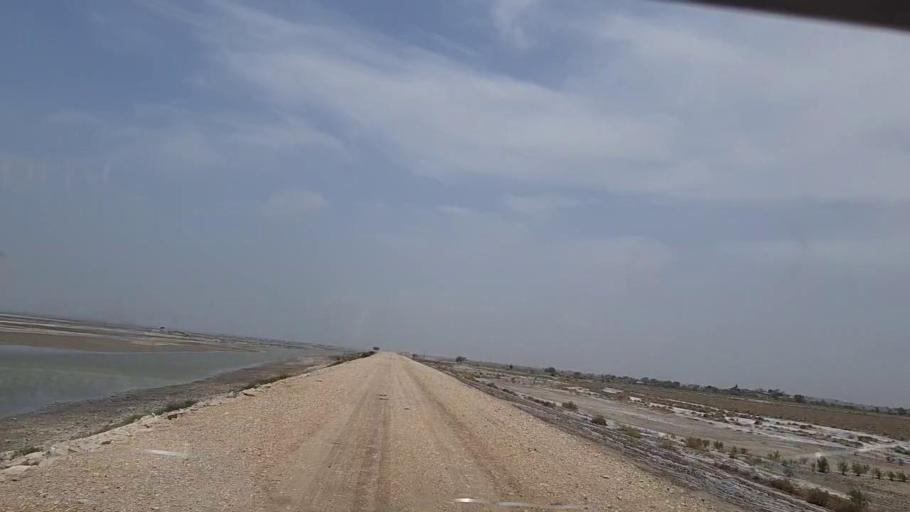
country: PK
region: Sindh
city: Sehwan
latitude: 26.4152
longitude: 67.7613
